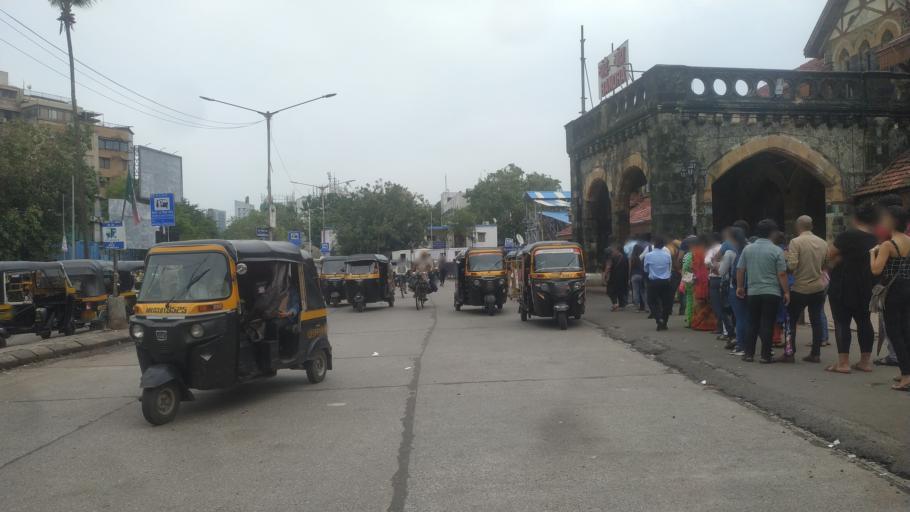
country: IN
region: Maharashtra
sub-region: Mumbai Suburban
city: Mumbai
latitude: 19.0549
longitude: 72.8400
